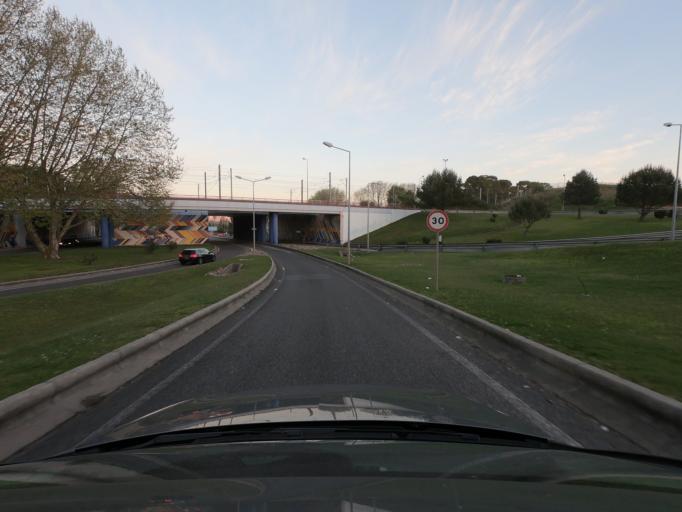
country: PT
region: Lisbon
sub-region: Sintra
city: Queluz
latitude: 38.7544
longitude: -9.2670
